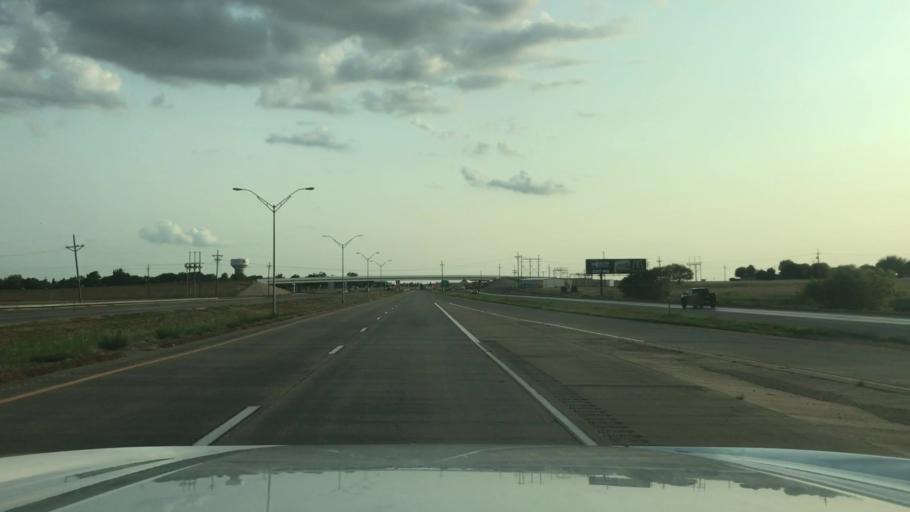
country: US
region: Texas
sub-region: Hale County
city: Plainview
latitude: 34.2075
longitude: -101.7388
